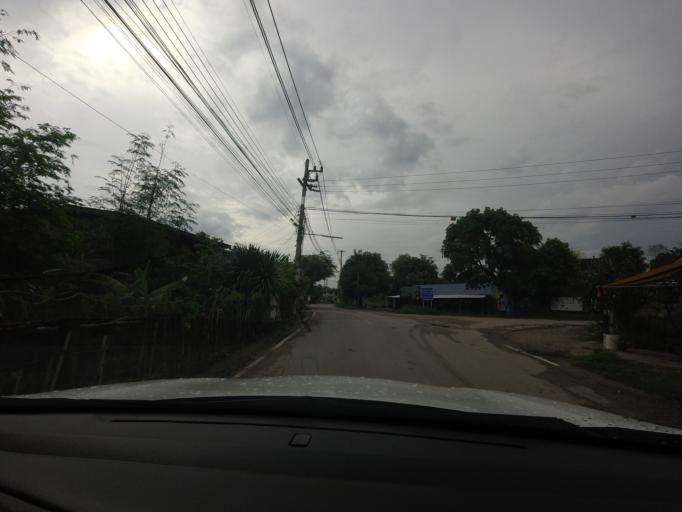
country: TH
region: Nakhon Ratchasima
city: Pak Chong
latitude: 14.6247
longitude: 101.4386
